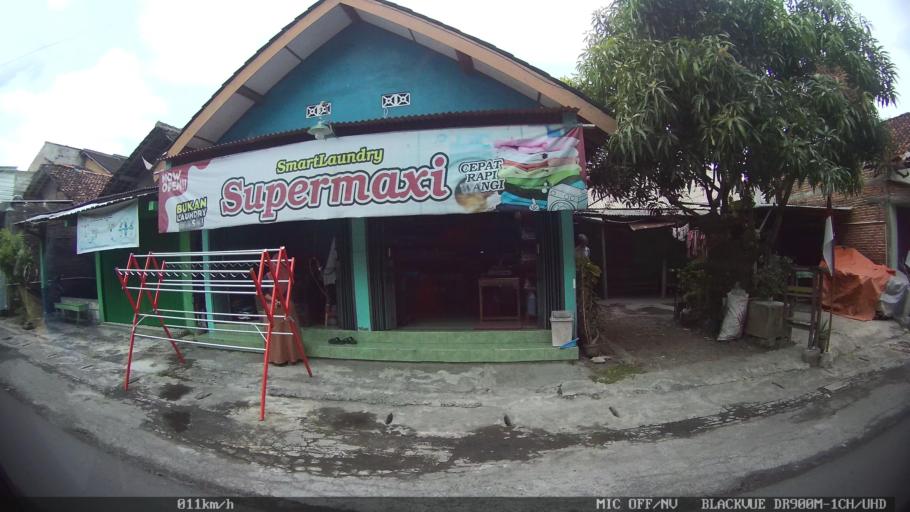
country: ID
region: Daerah Istimewa Yogyakarta
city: Depok
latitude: -7.8035
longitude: 110.4162
